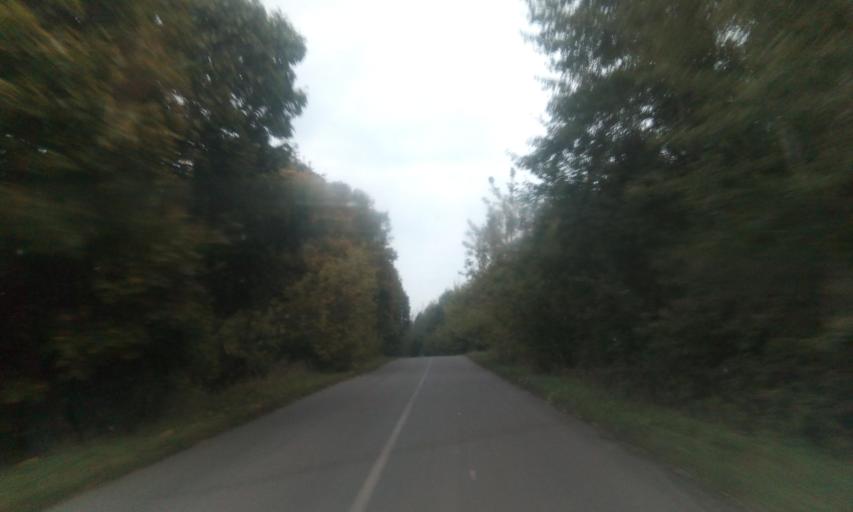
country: RU
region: Tula
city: Dubovka
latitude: 53.9568
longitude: 38.0618
